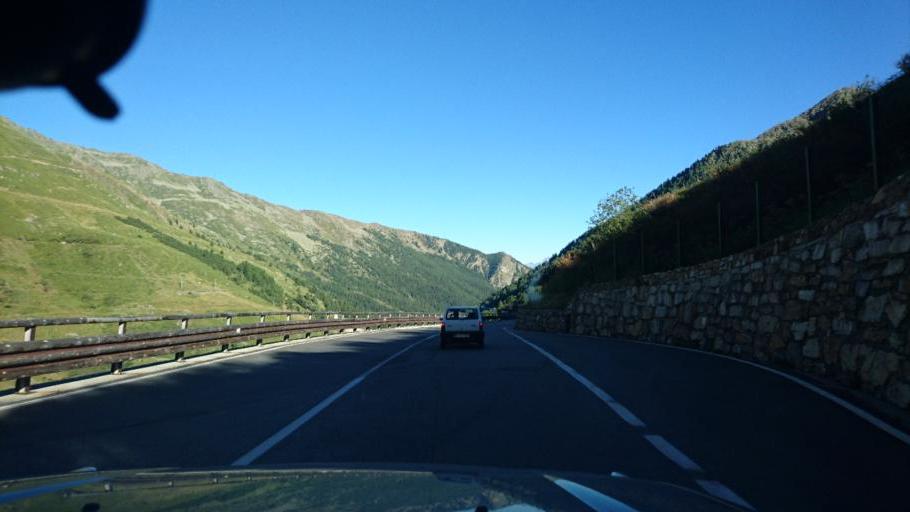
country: IT
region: Aosta Valley
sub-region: Valle d'Aosta
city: San Leonardo
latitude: 45.8543
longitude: 7.1509
